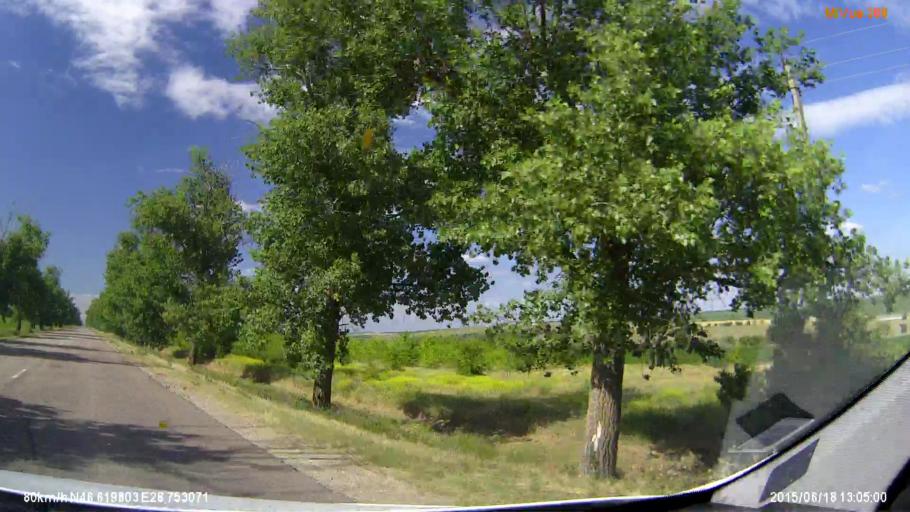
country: MD
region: Cimislia
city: Cimislia
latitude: 46.6196
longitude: 28.7531
